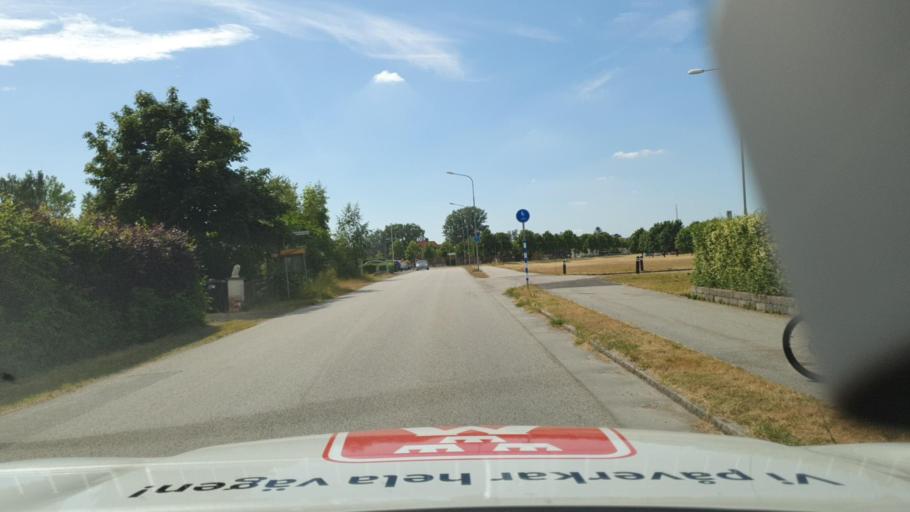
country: SE
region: Skane
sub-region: Sjobo Kommun
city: Sjoebo
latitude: 55.6287
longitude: 13.7147
